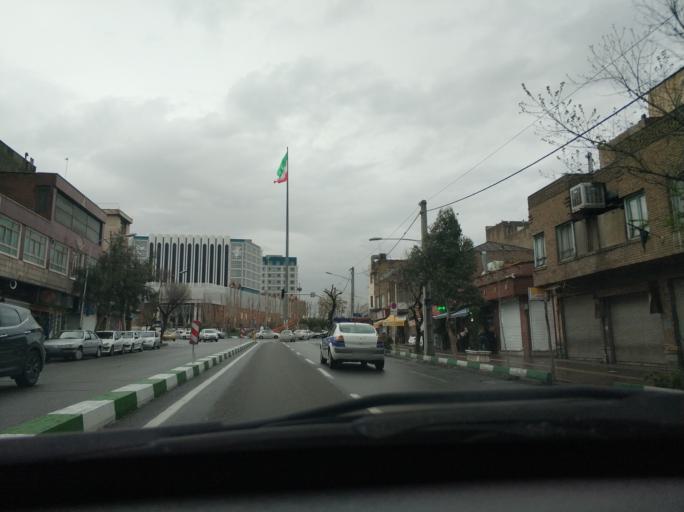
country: IR
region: Tehran
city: Tehran
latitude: 35.7056
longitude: 51.4400
